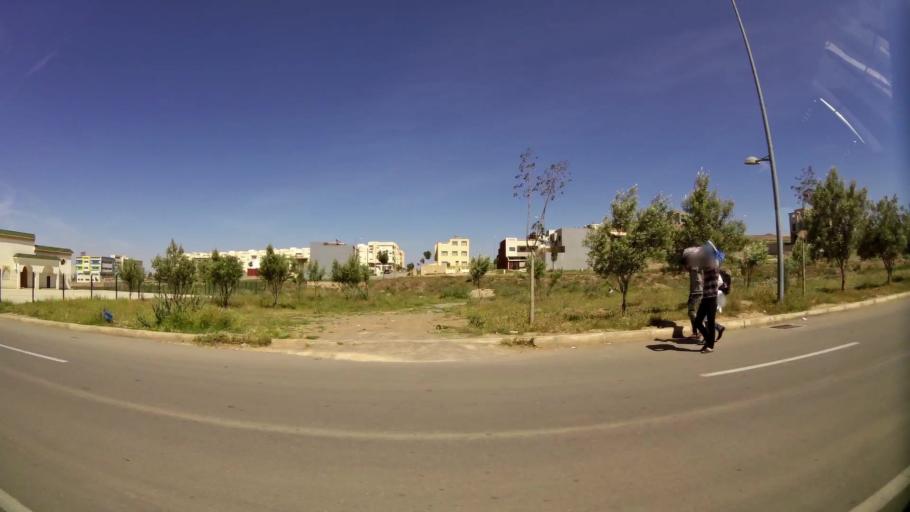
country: MA
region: Oriental
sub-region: Oujda-Angad
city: Oujda
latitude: 34.6530
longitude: -1.9134
